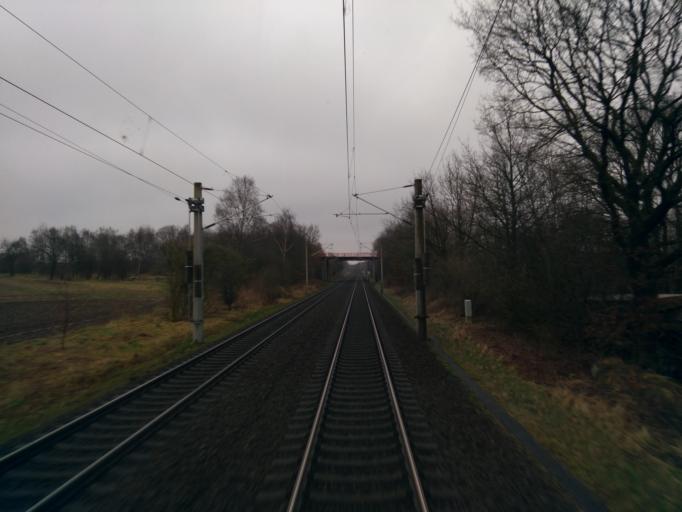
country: DE
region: Lower Saxony
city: Bendestorf
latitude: 53.3544
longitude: 9.9196
